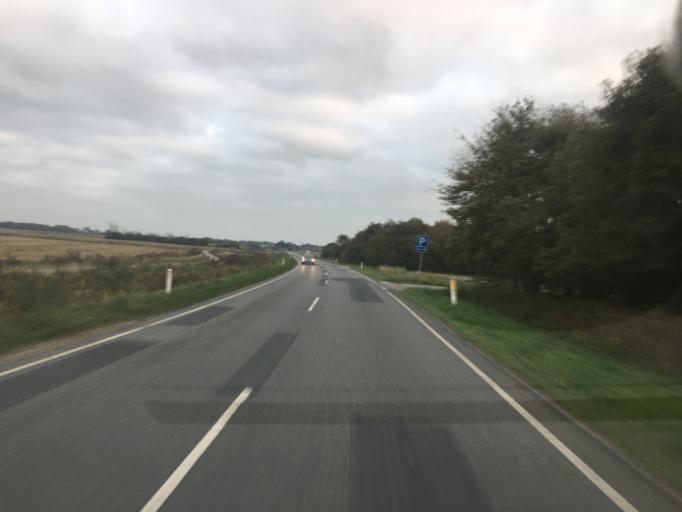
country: DE
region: Schleswig-Holstein
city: Aventoft
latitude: 54.9544
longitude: 8.7720
